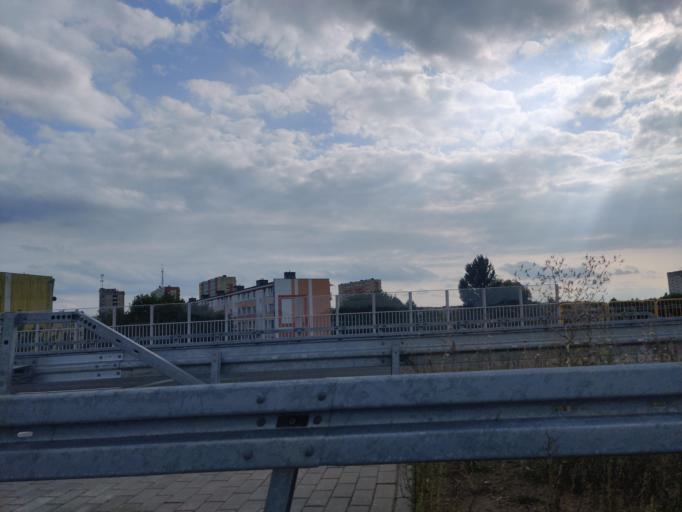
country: PL
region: Greater Poland Voivodeship
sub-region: Konin
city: Konin
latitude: 52.2339
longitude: 18.2734
